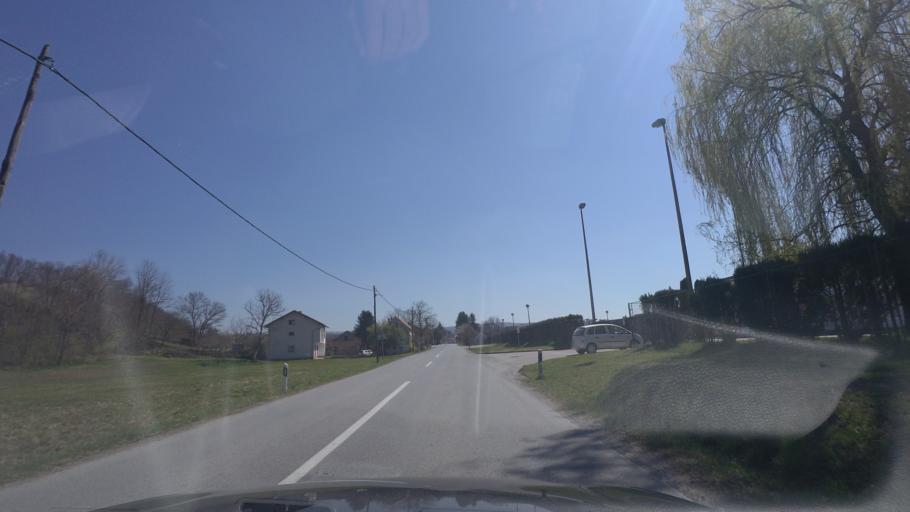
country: HR
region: Karlovacka
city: Vojnic
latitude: 45.3294
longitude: 15.6913
